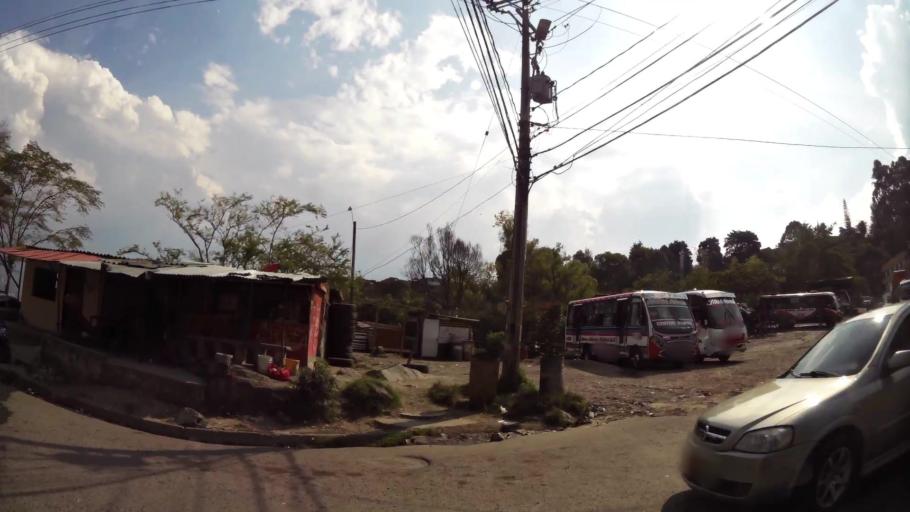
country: CO
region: Antioquia
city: Medellin
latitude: 6.2928
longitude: -75.5946
